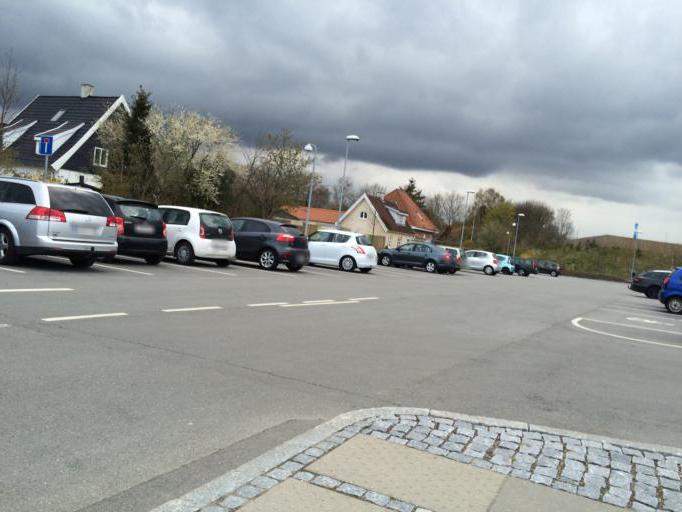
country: DK
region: Capital Region
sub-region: Hoje-Taastrup Kommune
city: Taastrup
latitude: 55.6513
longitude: 12.2992
